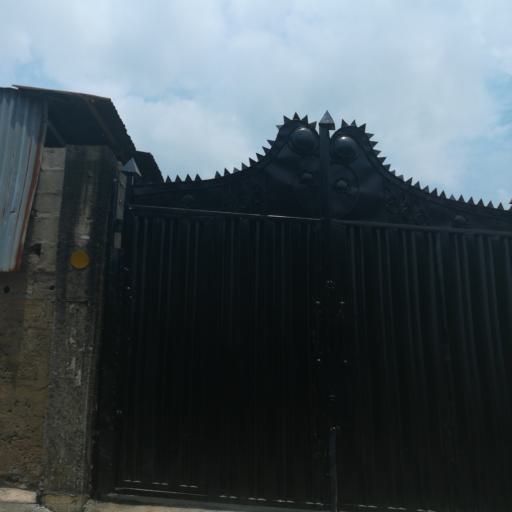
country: NG
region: Lagos
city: Ojota
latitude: 6.5807
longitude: 3.3818
